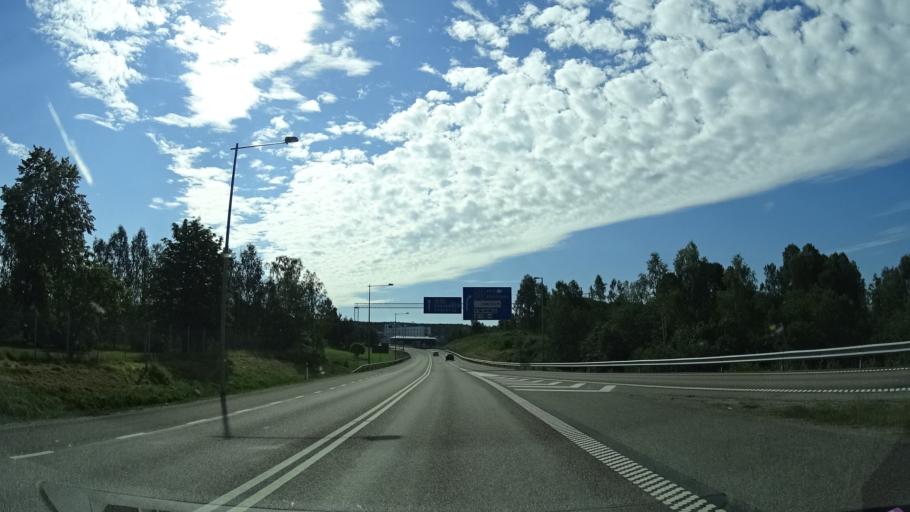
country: SE
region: Vaermland
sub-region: Arjangs Kommun
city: Arjaeng
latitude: 59.3975
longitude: 12.1267
